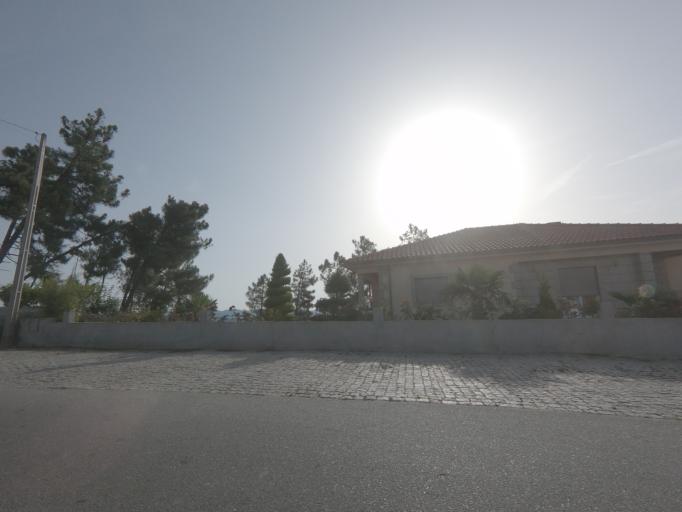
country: PT
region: Viseu
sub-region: Sao Joao da Pesqueira
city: Sao Joao da Pesqueira
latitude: 41.2326
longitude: -7.4664
